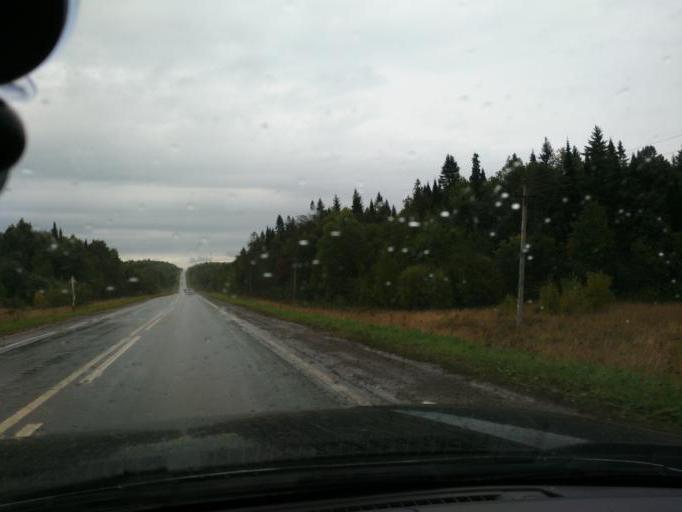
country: RU
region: Perm
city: Kultayevo
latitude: 57.8266
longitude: 55.8096
